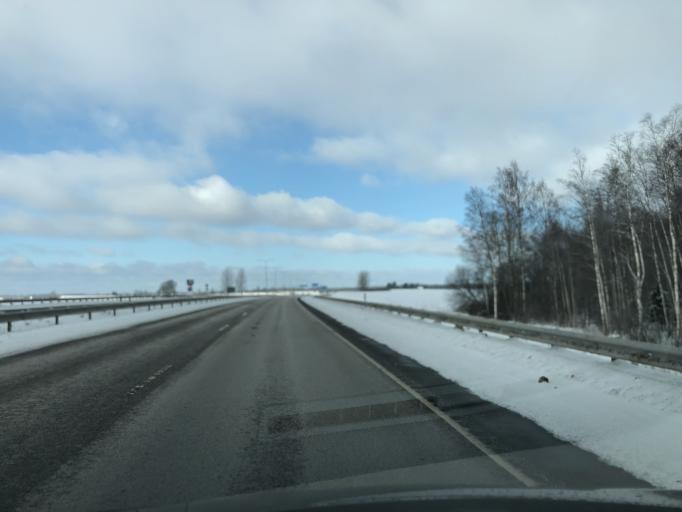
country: EE
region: Jaervamaa
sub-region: Paide linn
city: Paide
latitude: 58.9105
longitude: 25.6257
